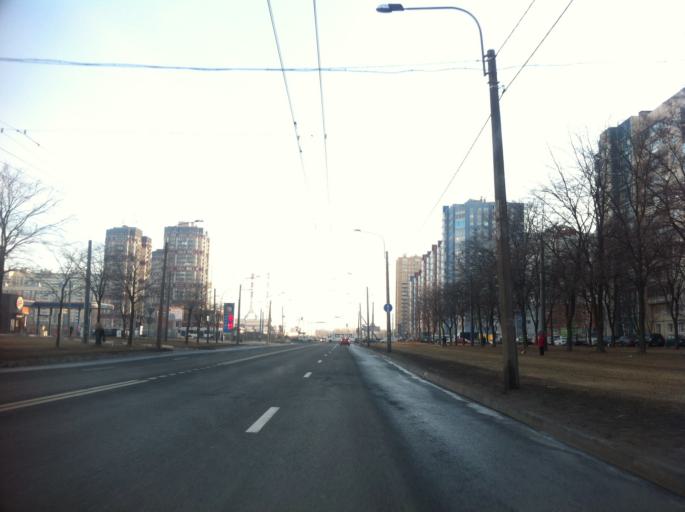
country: RU
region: St.-Petersburg
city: Uritsk
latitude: 59.8598
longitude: 30.1783
